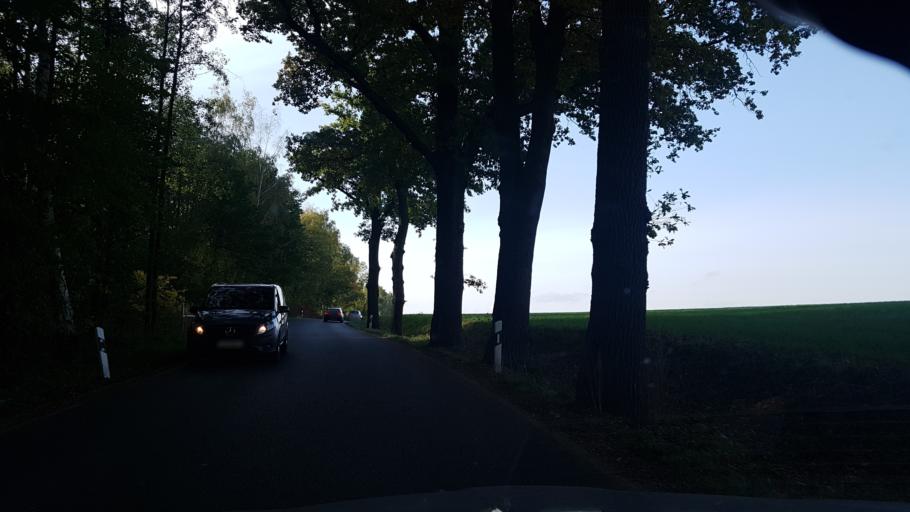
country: DE
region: Saxony
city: Struppen
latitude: 50.9275
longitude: 14.0343
